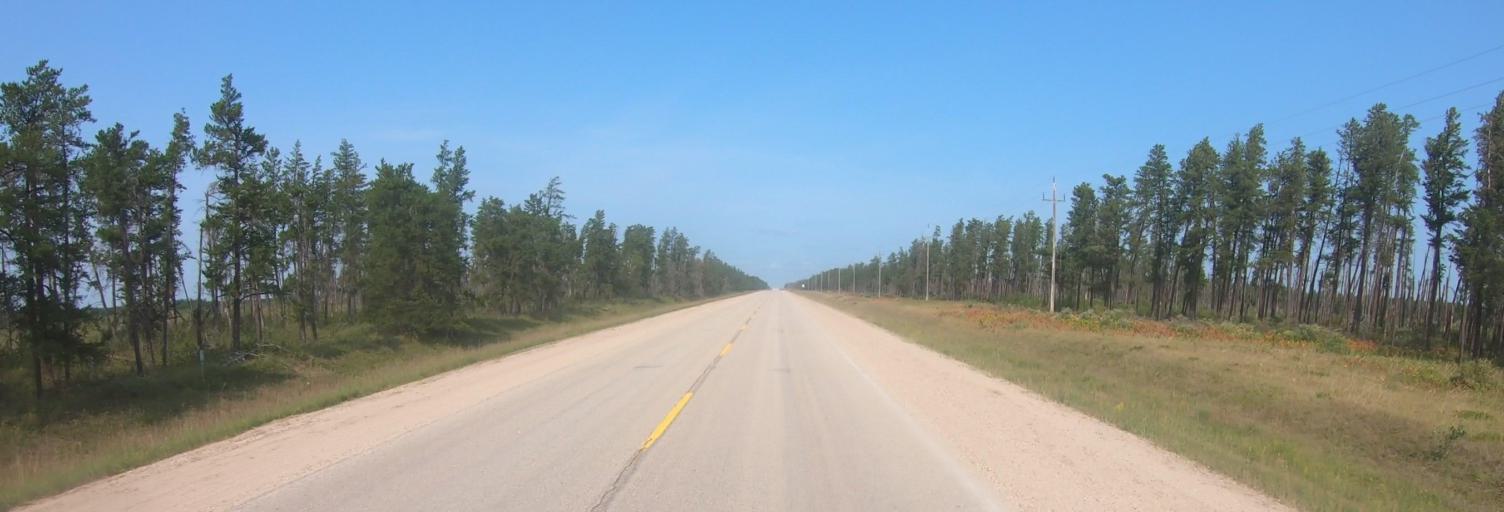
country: US
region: Minnesota
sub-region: Roseau County
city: Roseau
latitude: 49.1229
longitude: -96.0617
